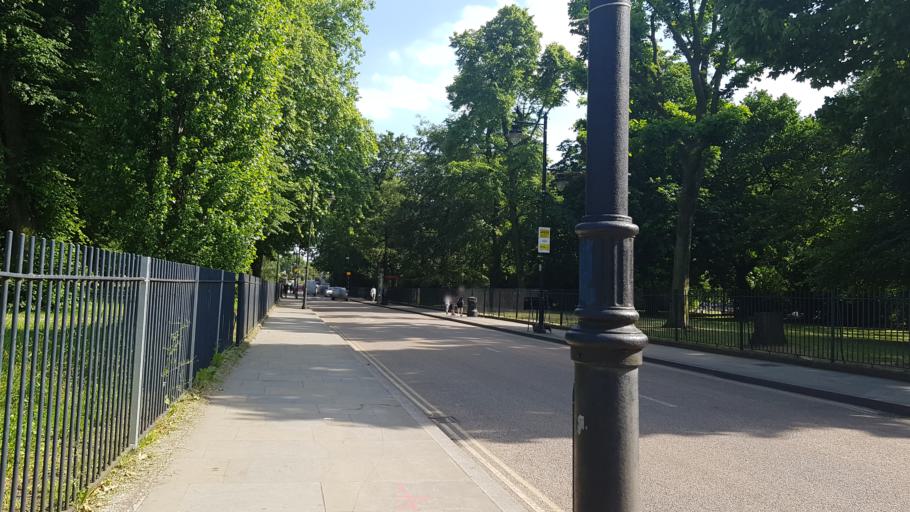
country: GB
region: England
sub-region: Greater London
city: Hackney
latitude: 51.5350
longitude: -0.0424
